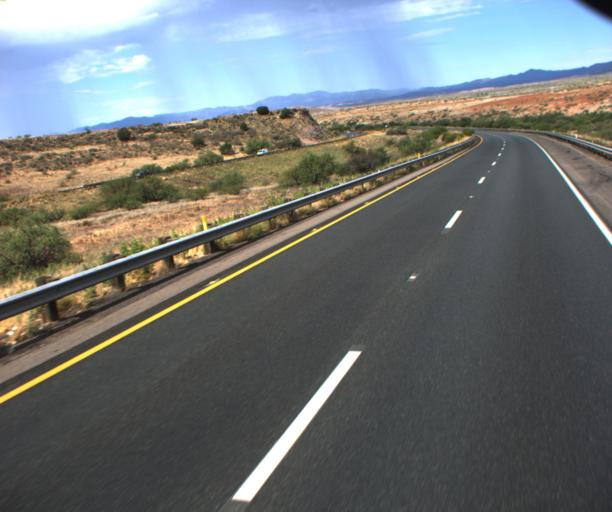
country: US
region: Arizona
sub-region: Yavapai County
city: Cordes Lakes
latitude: 34.4227
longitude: -112.0576
